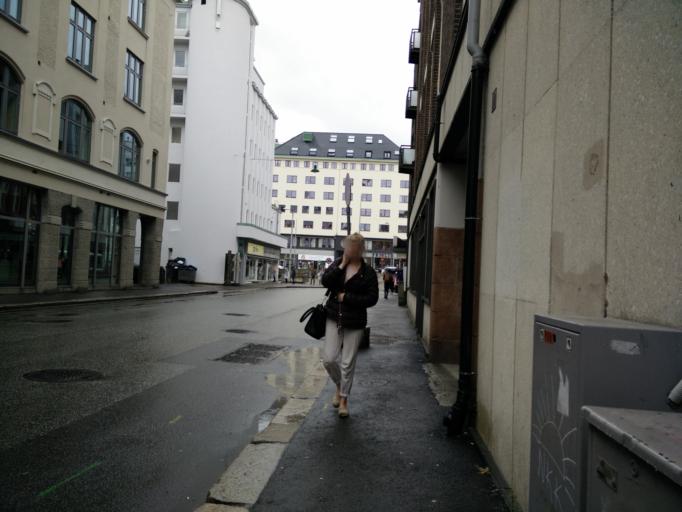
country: NO
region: Hordaland
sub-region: Bergen
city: Bergen
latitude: 60.3957
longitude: 5.3190
